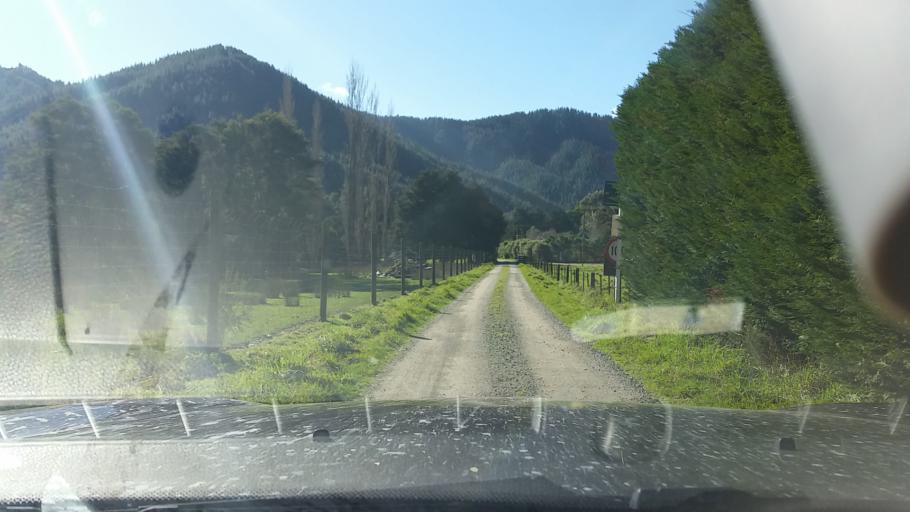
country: NZ
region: Marlborough
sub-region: Marlborough District
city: Blenheim
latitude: -41.4044
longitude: 173.7340
